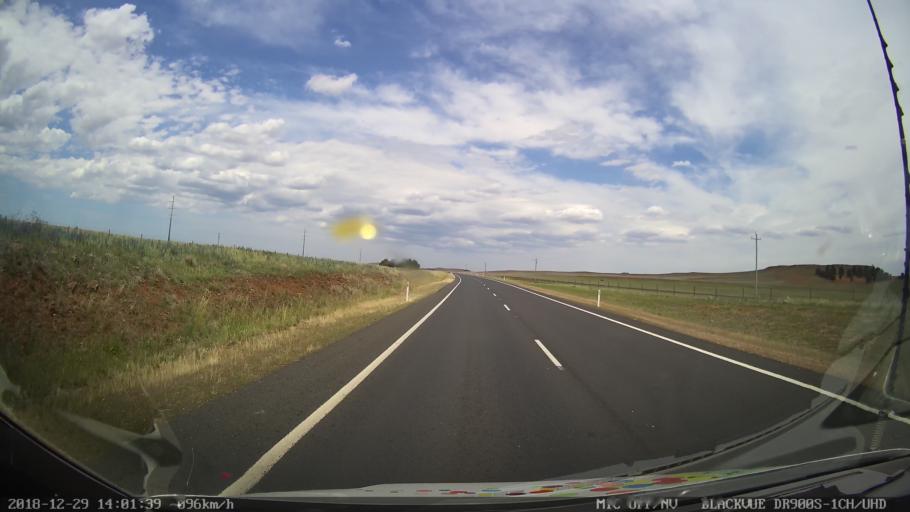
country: AU
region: New South Wales
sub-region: Cooma-Monaro
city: Cooma
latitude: -36.2783
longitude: 149.1693
